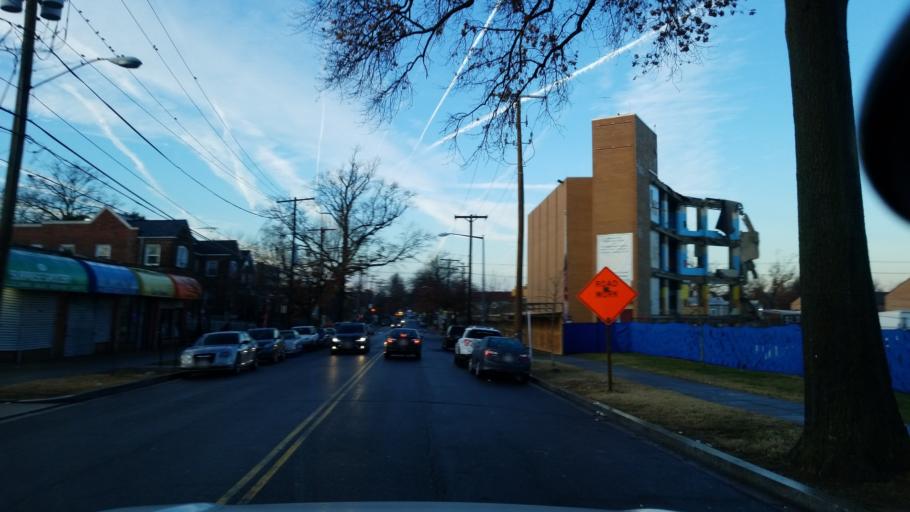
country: US
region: Maryland
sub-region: Prince George's County
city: Silver Hill
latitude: 38.8721
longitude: -76.9736
